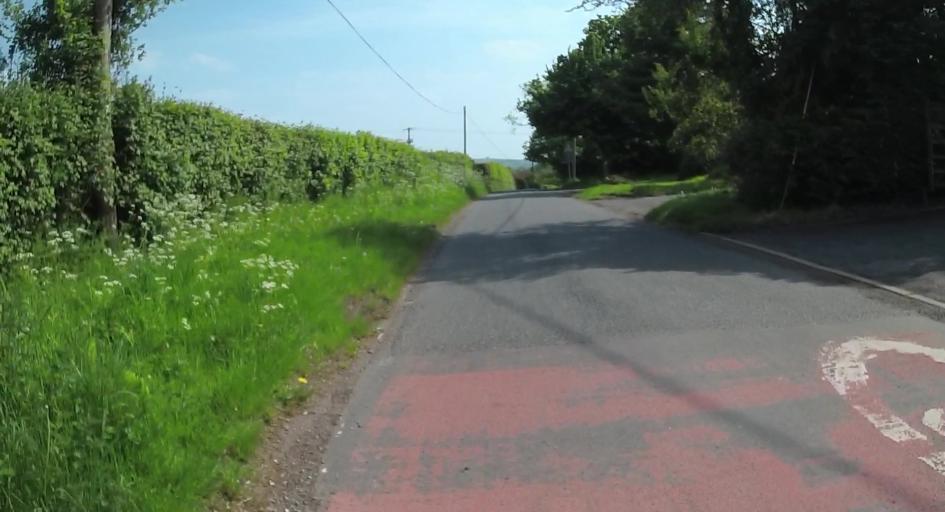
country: GB
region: England
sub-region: West Berkshire
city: Greenham
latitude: 51.3462
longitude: -1.3229
